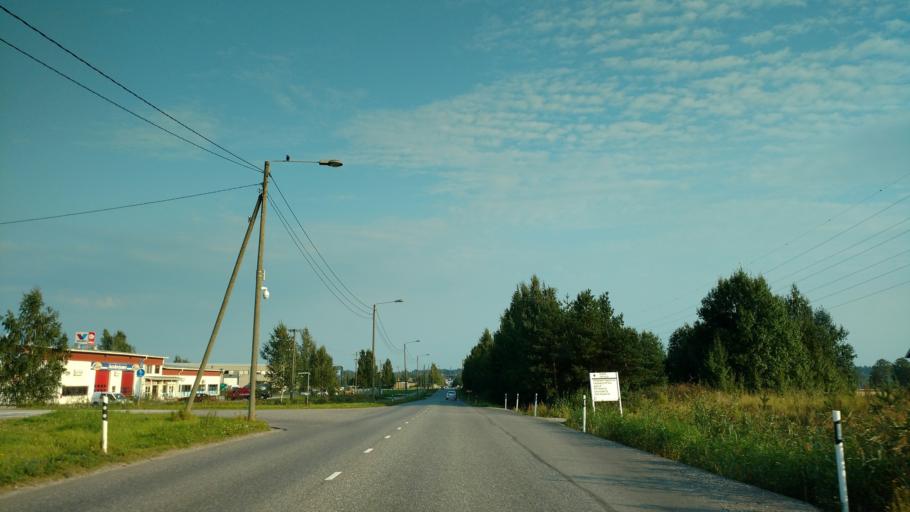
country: FI
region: Varsinais-Suomi
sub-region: Salo
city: Halikko
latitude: 60.3870
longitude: 23.0969
